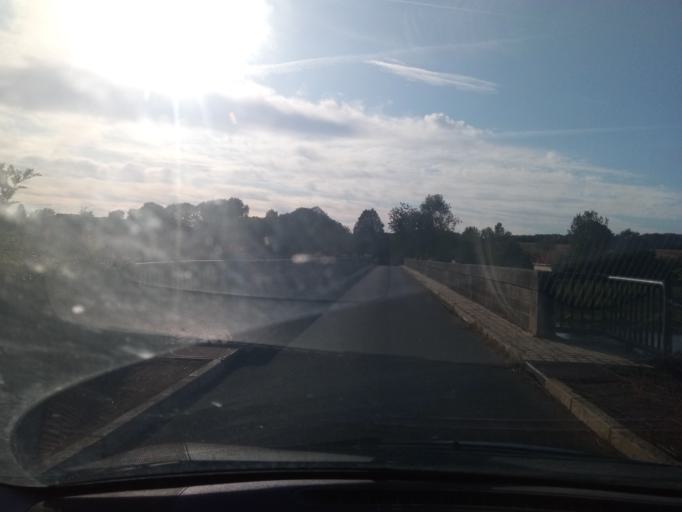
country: FR
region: Poitou-Charentes
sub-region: Departement de la Vienne
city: Montmorillon
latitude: 46.4907
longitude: 0.8378
